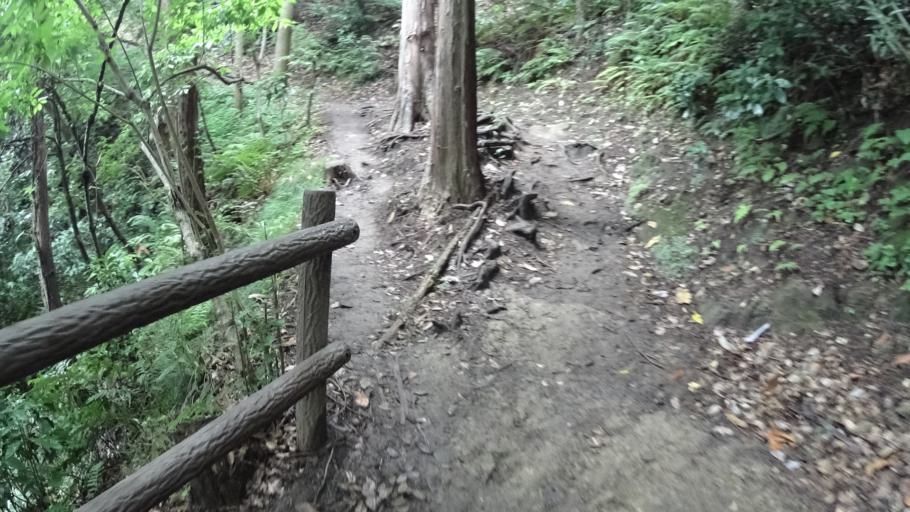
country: JP
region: Kanagawa
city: Zushi
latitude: 35.3545
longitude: 139.6145
